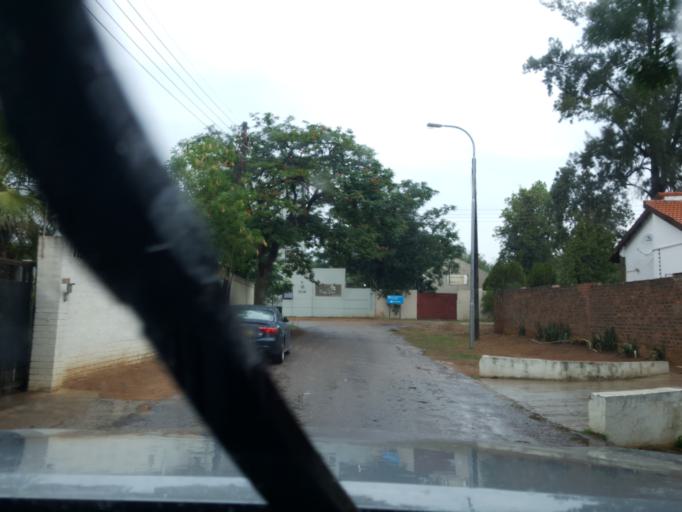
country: BW
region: South East
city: Gaborone
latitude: -24.6419
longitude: 25.9226
